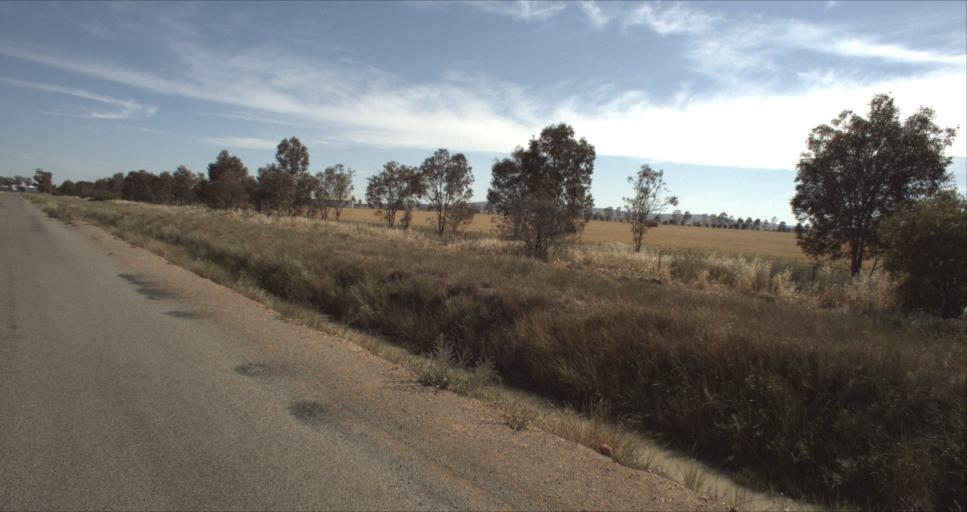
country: AU
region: New South Wales
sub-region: Leeton
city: Leeton
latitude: -34.5646
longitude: 146.4708
